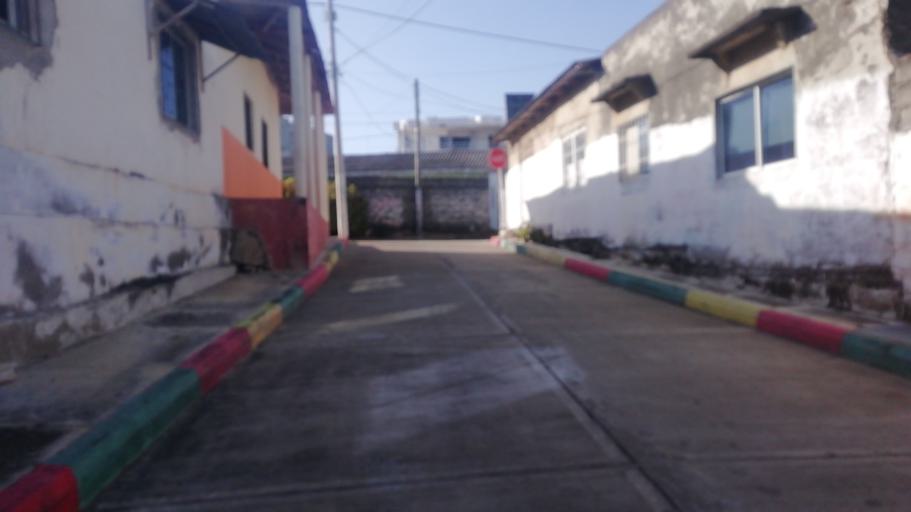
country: CO
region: Cordoba
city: San Antero
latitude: 9.3723
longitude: -75.7619
